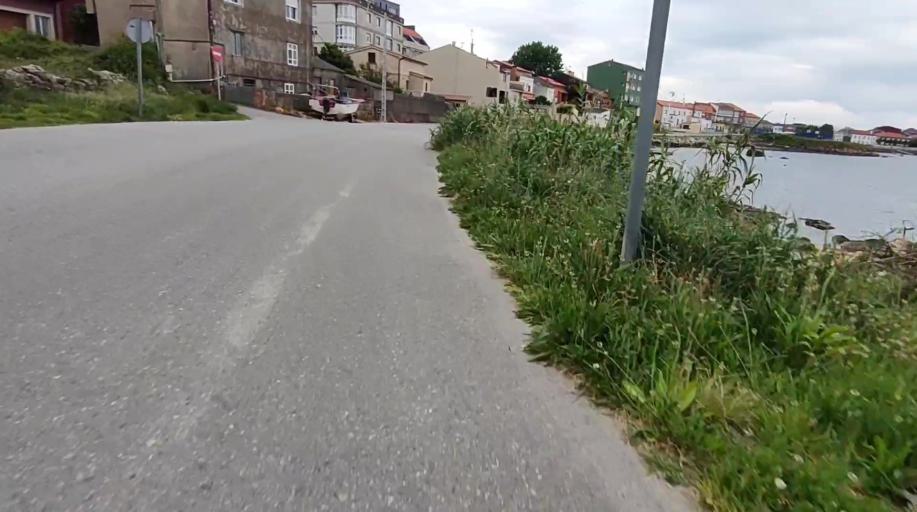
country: ES
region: Galicia
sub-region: Provincia da Coruna
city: Boiro
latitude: 42.6187
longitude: -8.8867
